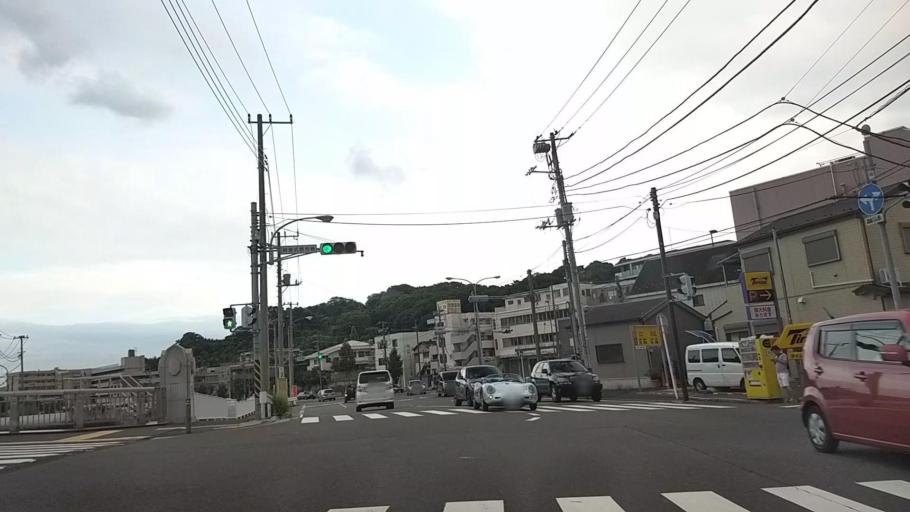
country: JP
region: Kanagawa
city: Yokohama
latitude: 35.4312
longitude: 139.6210
